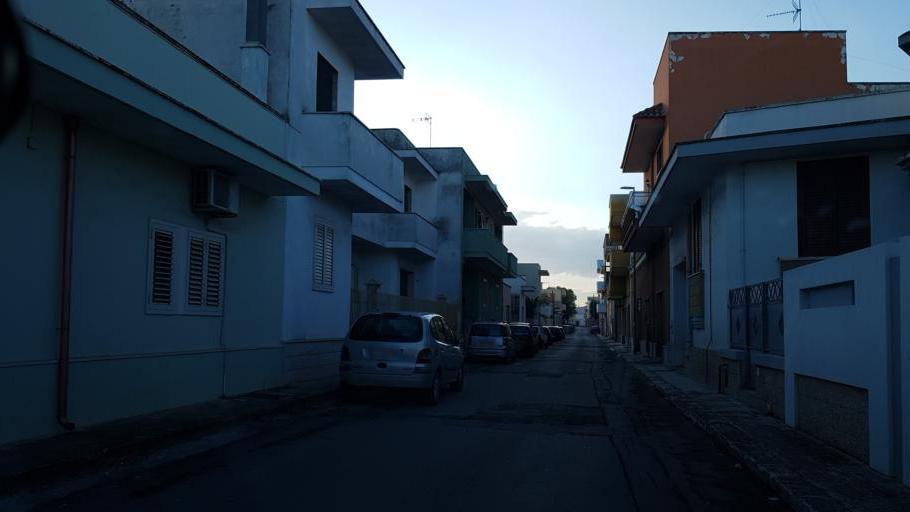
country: IT
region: Apulia
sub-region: Provincia di Lecce
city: Surbo
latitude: 40.3984
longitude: 18.1355
